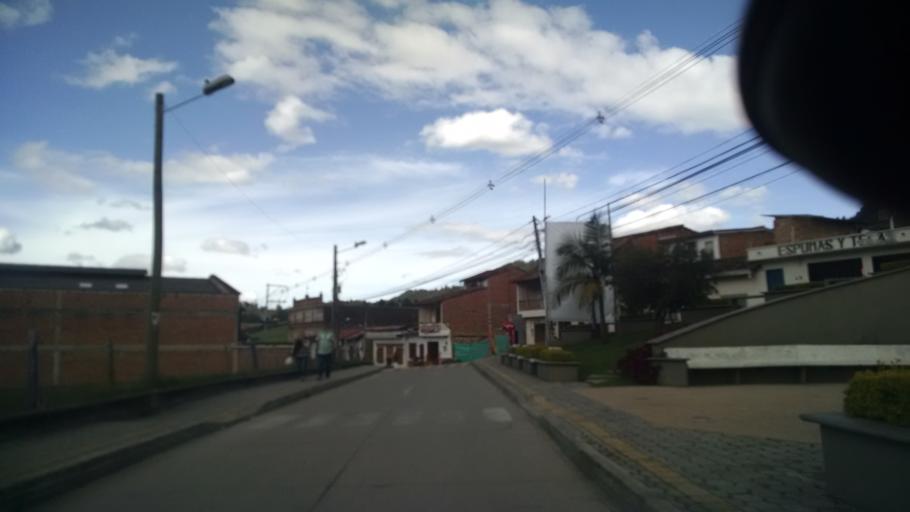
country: CO
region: Antioquia
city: El Retiro
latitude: 6.0606
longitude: -75.5030
